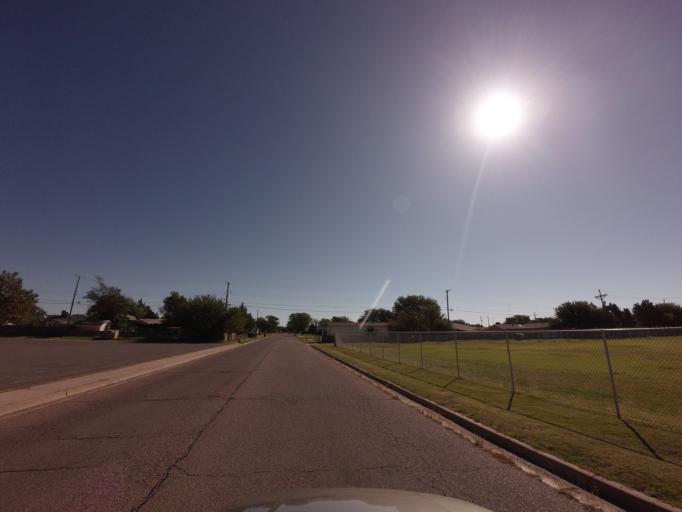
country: US
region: New Mexico
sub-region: Curry County
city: Clovis
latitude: 34.4278
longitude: -103.2235
